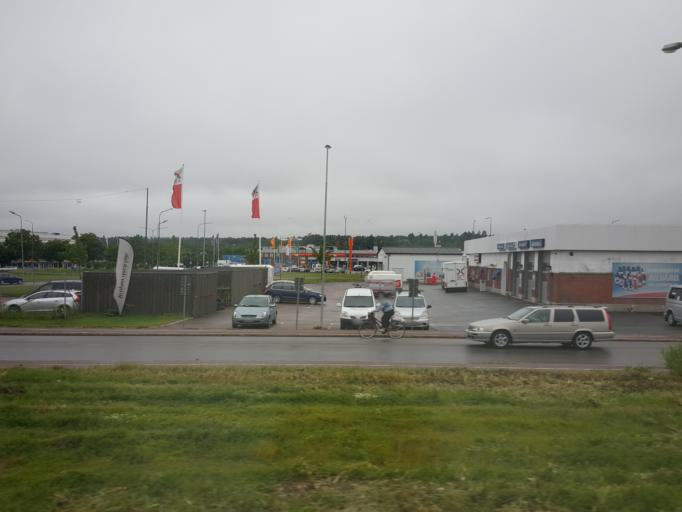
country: SE
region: Uppsala
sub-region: Uppsala Kommun
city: Uppsala
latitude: 59.8483
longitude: 17.6658
